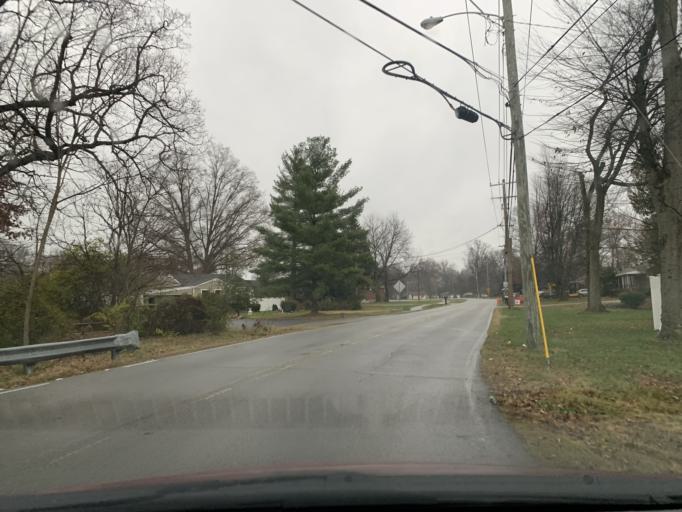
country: US
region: Kentucky
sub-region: Jefferson County
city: Buechel
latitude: 38.1991
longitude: -85.6434
